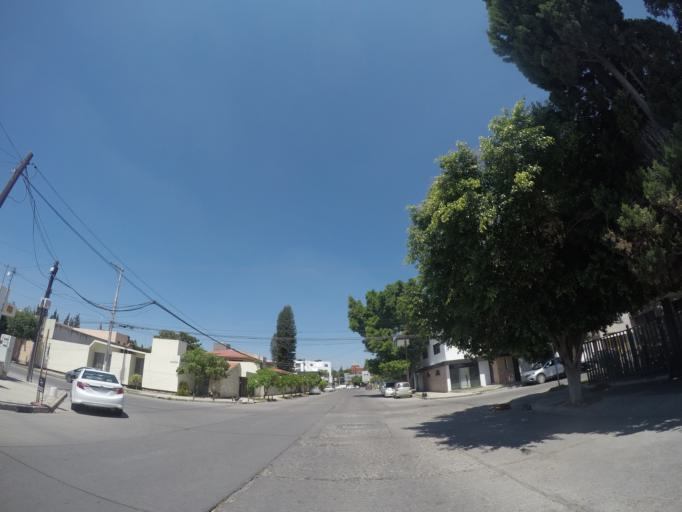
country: MX
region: San Luis Potosi
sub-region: San Luis Potosi
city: San Luis Potosi
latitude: 22.1470
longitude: -101.0026
